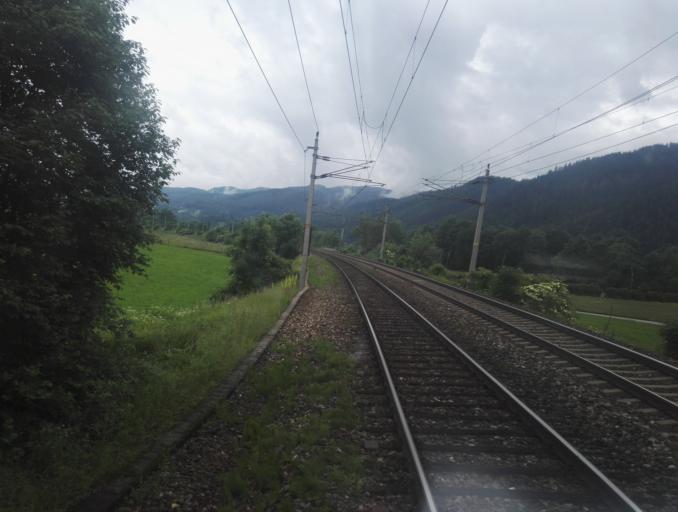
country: AT
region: Styria
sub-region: Politischer Bezirk Bruck-Muerzzuschlag
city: Krieglach
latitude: 47.5477
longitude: 15.5377
